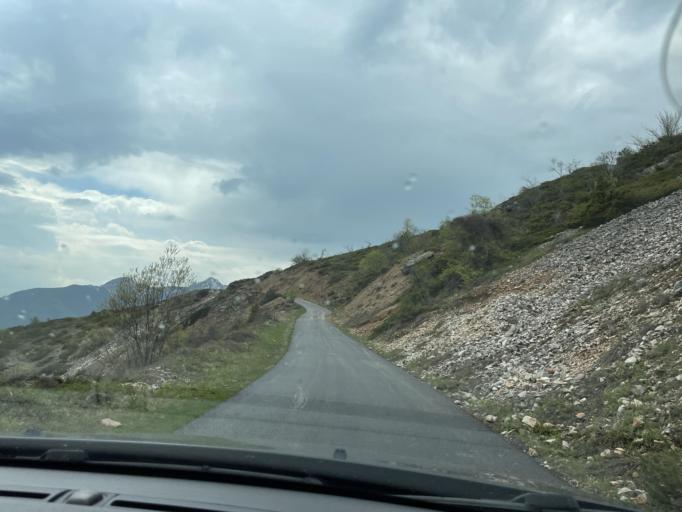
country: MK
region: Opstina Rostusa
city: Rostusha
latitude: 41.5938
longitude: 20.6640
